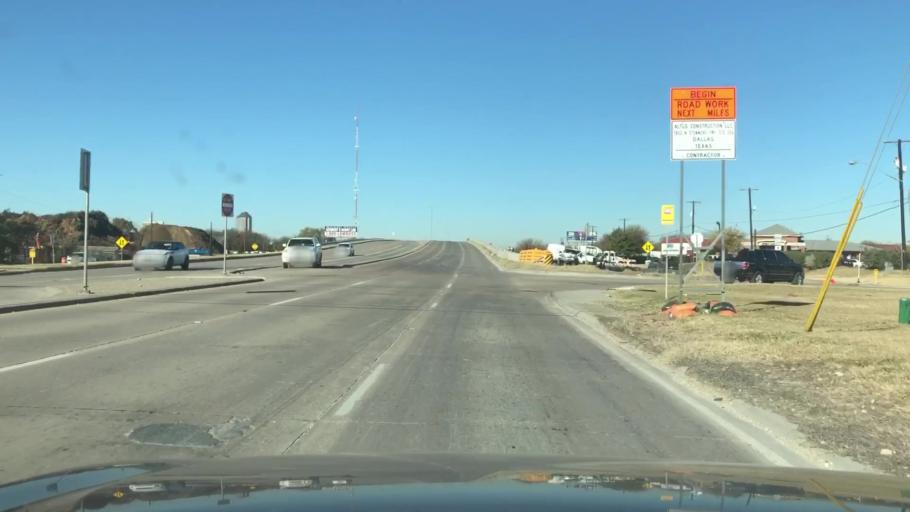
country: US
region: Texas
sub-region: Dallas County
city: Farmers Branch
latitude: 32.8688
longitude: -96.9127
